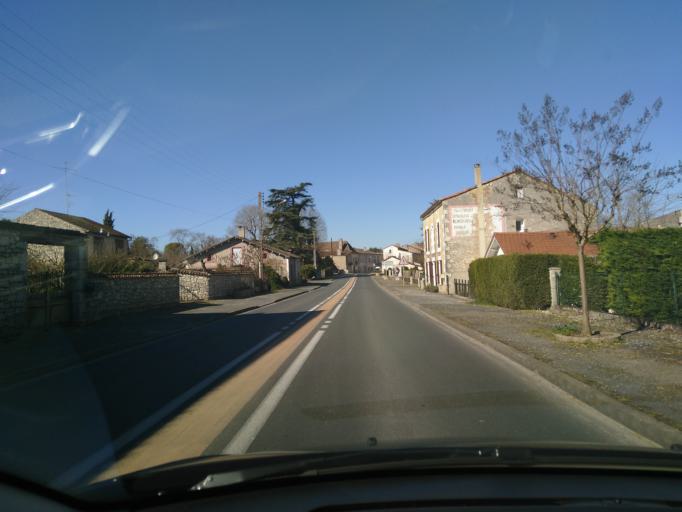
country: FR
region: Aquitaine
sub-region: Departement de la Dordogne
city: Monbazillac
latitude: 44.7569
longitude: 0.5279
